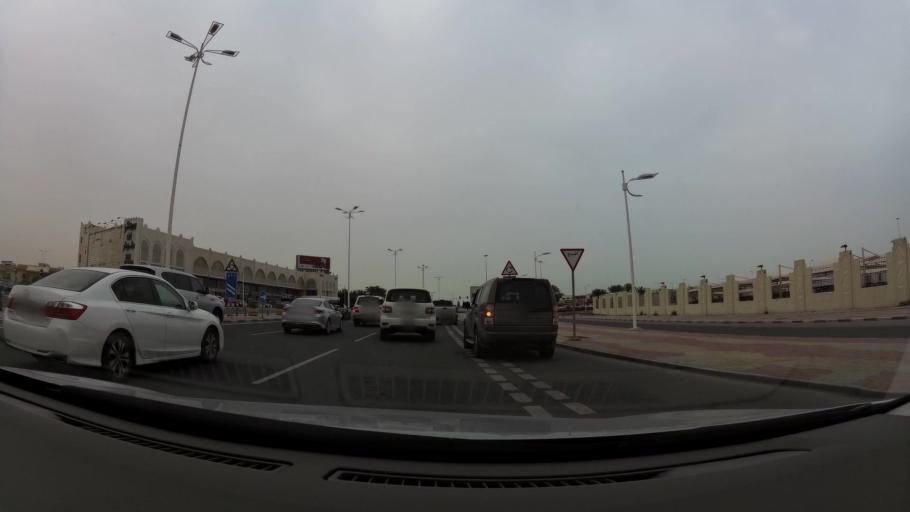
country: QA
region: Baladiyat ad Dawhah
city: Doha
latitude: 25.3155
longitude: 51.4956
